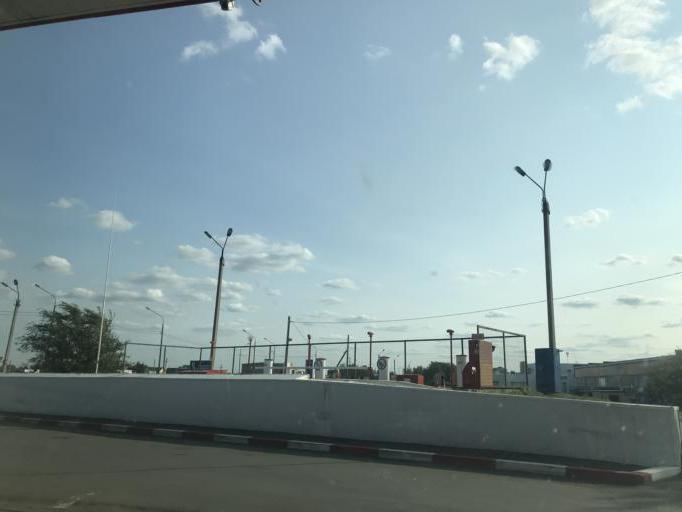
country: RU
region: Chelyabinsk
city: Yuzhnoural'sk
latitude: 54.4553
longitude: 61.2795
